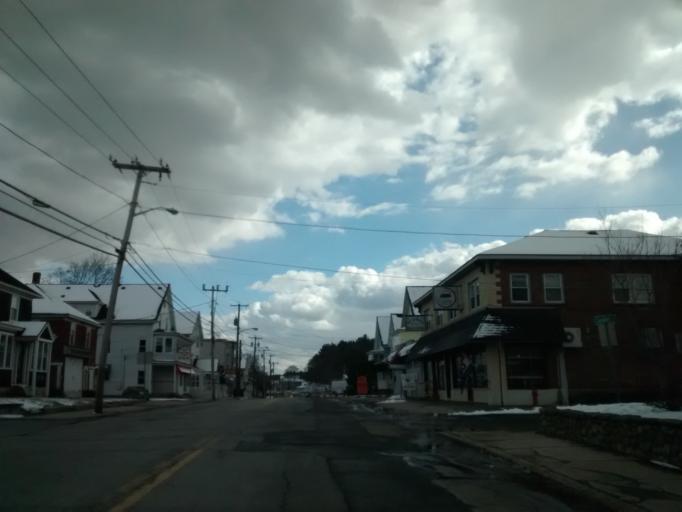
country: US
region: Massachusetts
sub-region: Worcester County
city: Uxbridge
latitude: 42.0906
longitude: -71.6429
